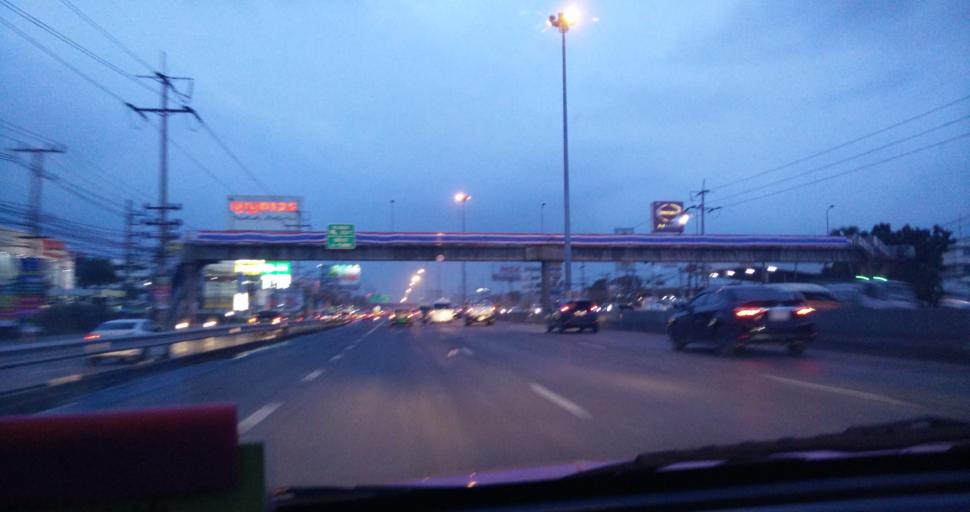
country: TH
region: Pathum Thani
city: Khlong Luang
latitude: 14.0250
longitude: 100.6157
